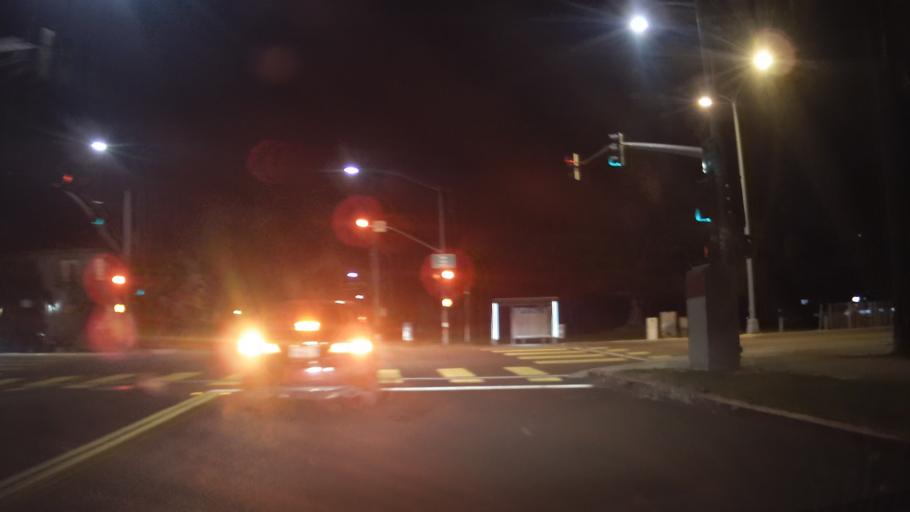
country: US
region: California
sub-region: San Diego County
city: San Diego
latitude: 32.7411
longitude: -117.1479
